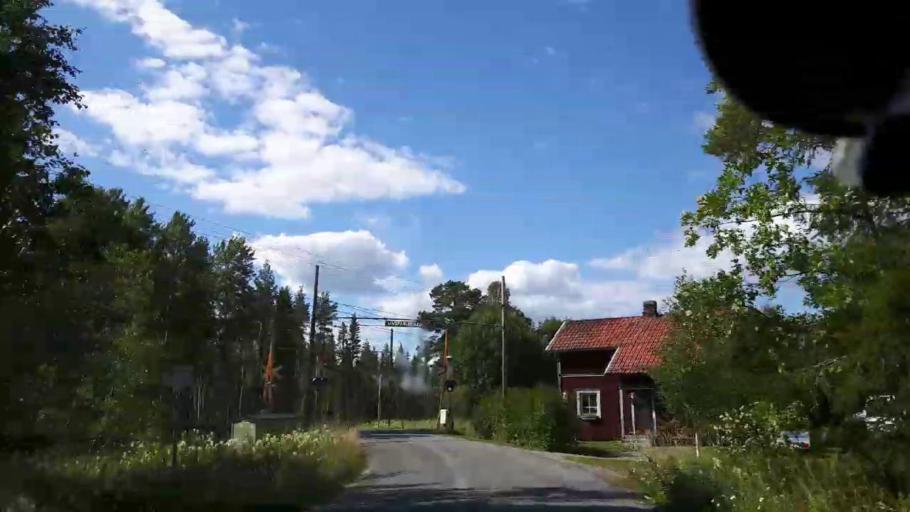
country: SE
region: Jaemtland
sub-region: Braecke Kommun
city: Braecke
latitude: 62.8398
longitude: 15.3009
